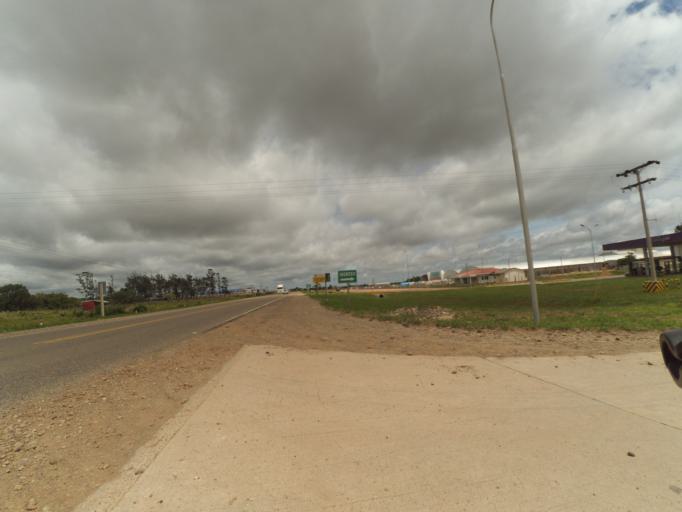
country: BO
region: Santa Cruz
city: Santa Rita
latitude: -17.8982
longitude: -63.2581
